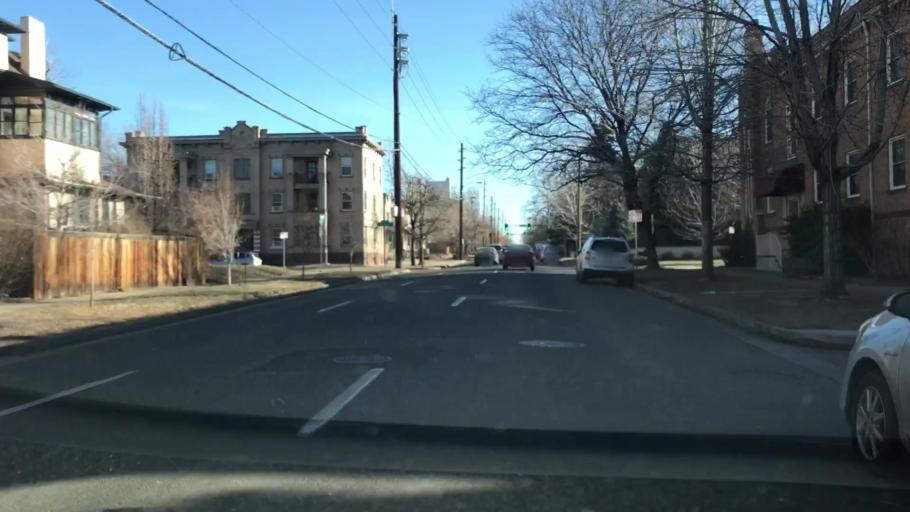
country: US
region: Colorado
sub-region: Denver County
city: Denver
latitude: 39.7384
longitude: -104.9617
